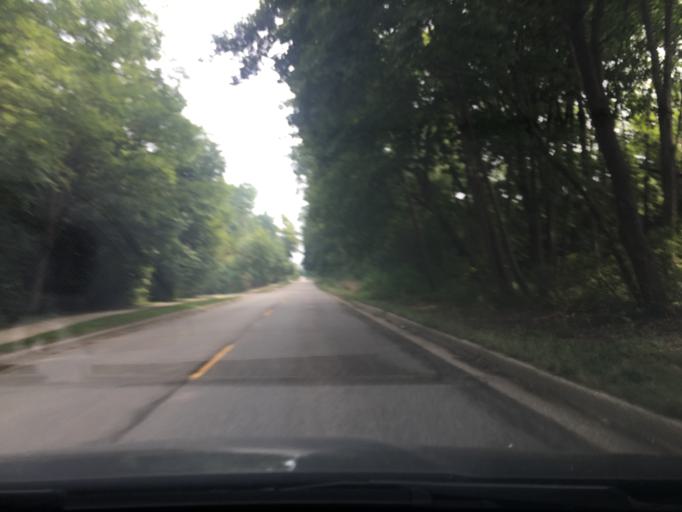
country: US
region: Michigan
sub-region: Oakland County
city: Birmingham
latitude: 42.5705
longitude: -83.2197
